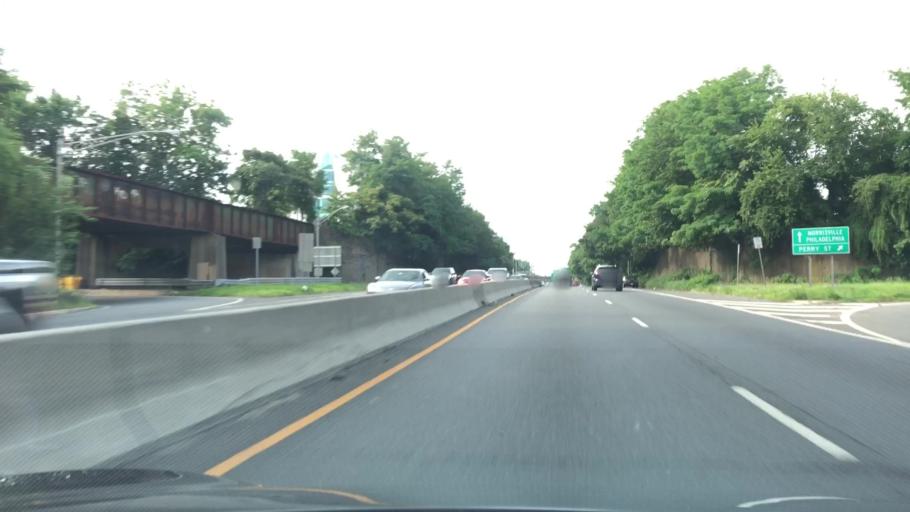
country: US
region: New Jersey
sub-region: Mercer County
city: Trenton
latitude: 40.2241
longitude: -74.7589
